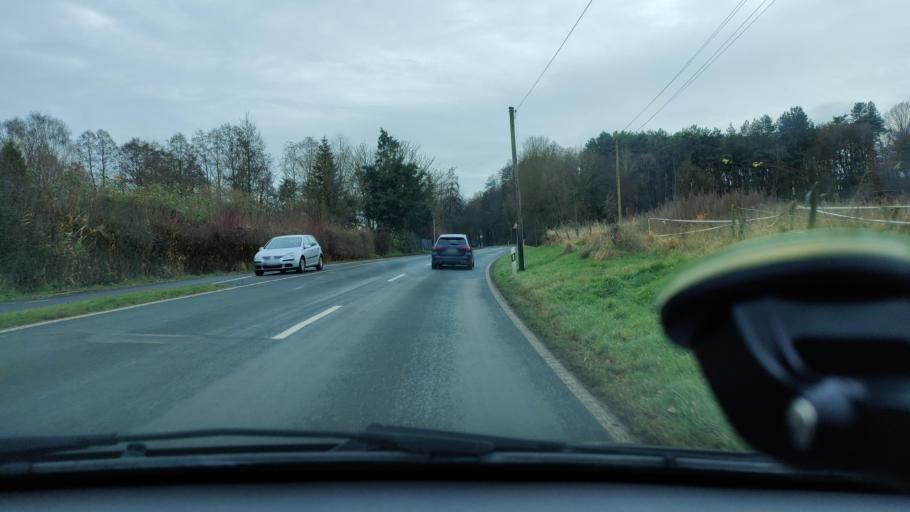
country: DE
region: North Rhine-Westphalia
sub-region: Regierungsbezirk Dusseldorf
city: Xanten
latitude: 51.6273
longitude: 6.4153
